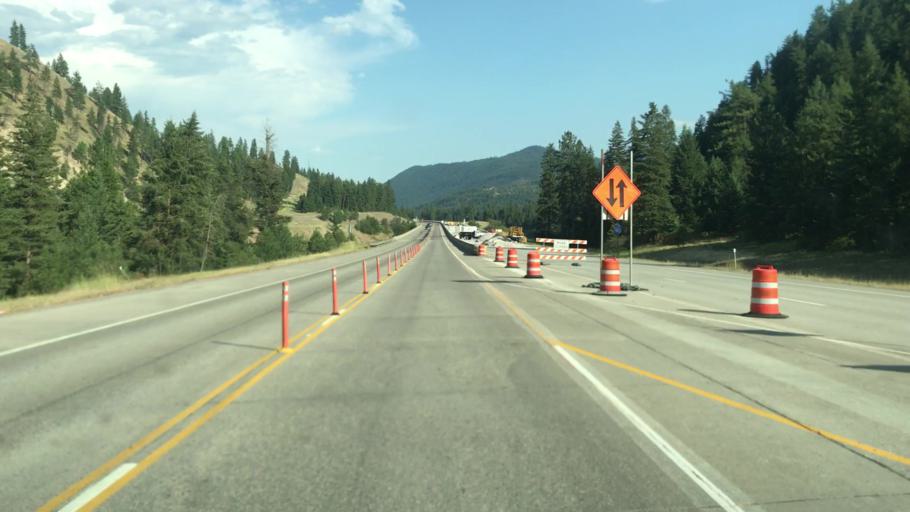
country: US
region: Montana
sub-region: Mineral County
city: Superior
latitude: 47.2231
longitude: -114.9646
